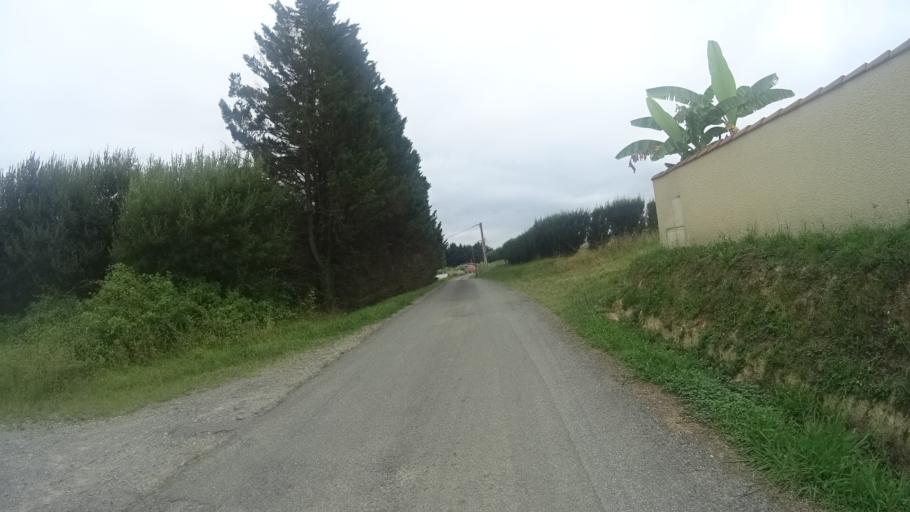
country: FR
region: Aquitaine
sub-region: Departement des Pyrenees-Atlantiques
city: Mont
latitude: 43.4881
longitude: -0.6950
